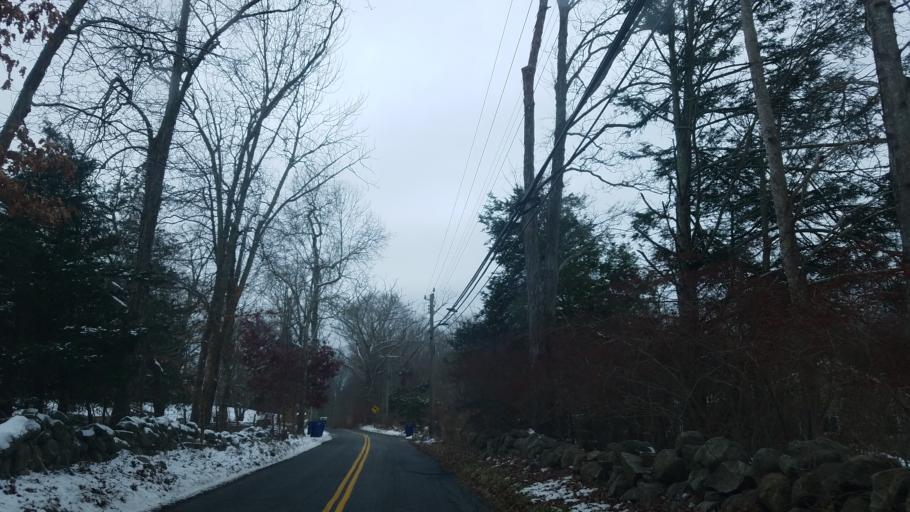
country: US
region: Connecticut
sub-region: New London County
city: Niantic
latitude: 41.3788
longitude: -72.1876
